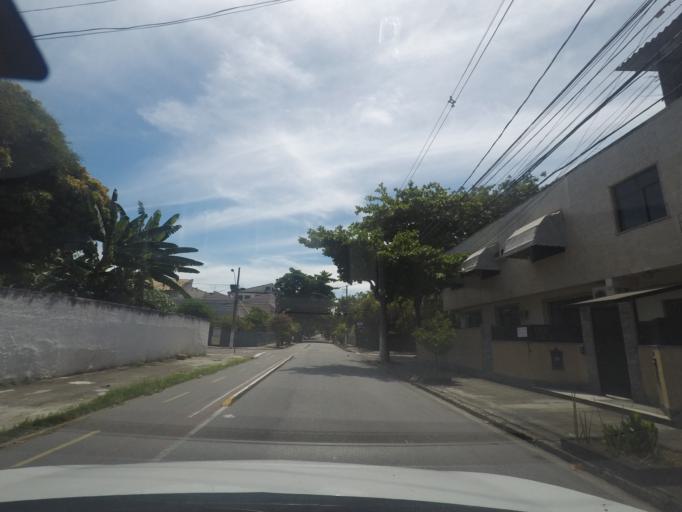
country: BR
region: Rio de Janeiro
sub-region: Niteroi
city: Niteroi
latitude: -22.9154
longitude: -43.0894
